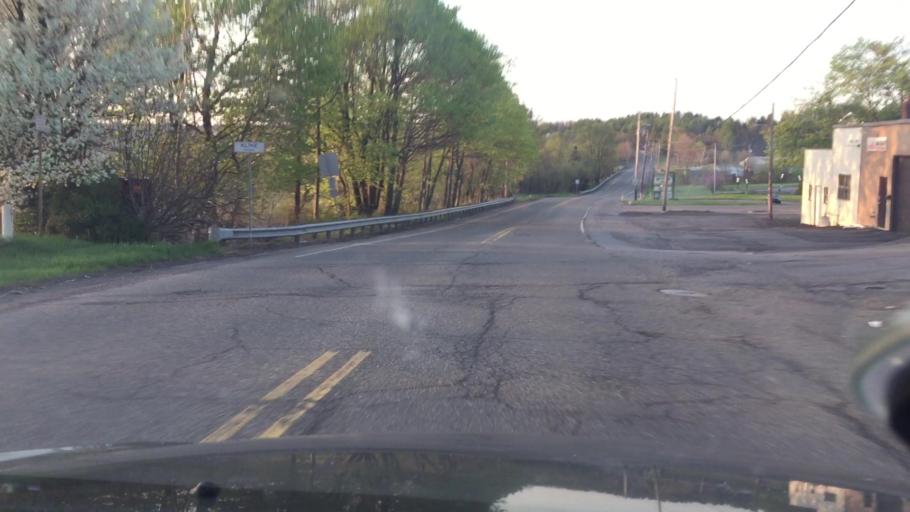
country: US
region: Pennsylvania
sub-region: Schuylkill County
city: McAdoo
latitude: 40.9051
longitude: -75.9930
